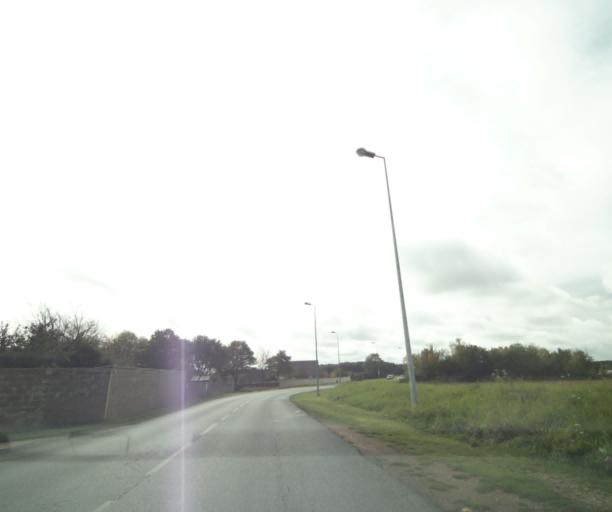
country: FR
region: Centre
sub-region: Departement d'Eure-et-Loir
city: Dreux
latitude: 48.7404
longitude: 1.3361
